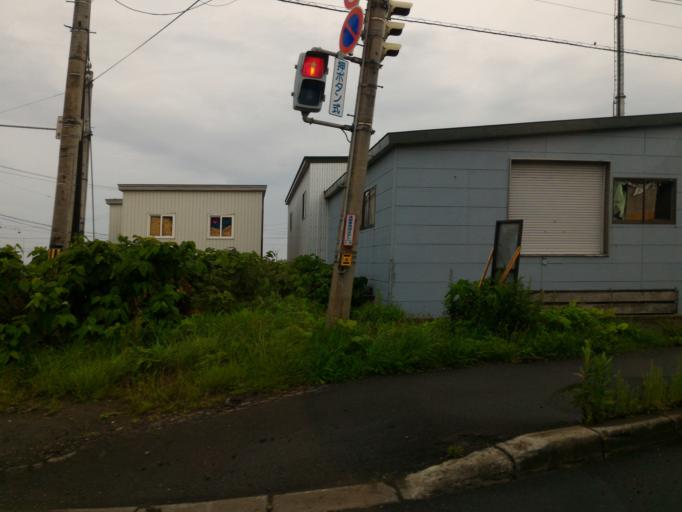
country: JP
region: Hokkaido
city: Rumoi
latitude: 43.9968
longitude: 141.6524
